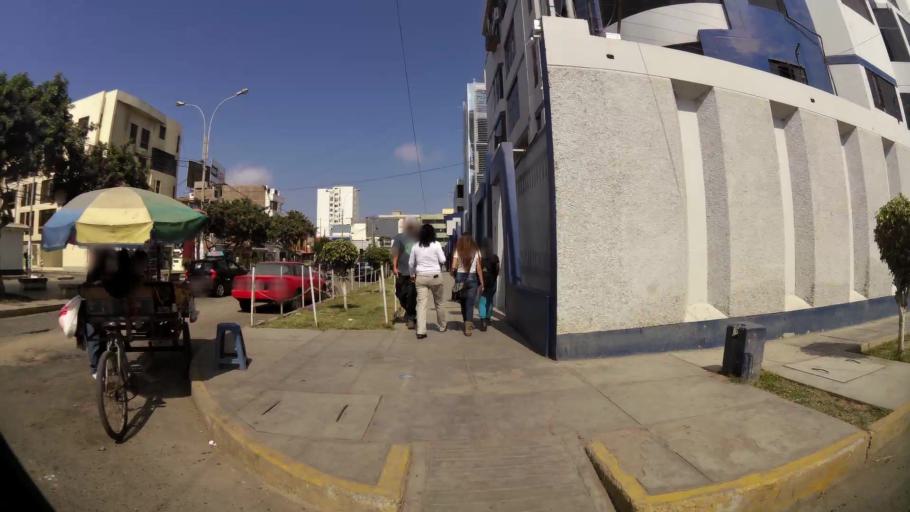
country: PE
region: La Libertad
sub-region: Provincia de Trujillo
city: Buenos Aires
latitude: -8.1281
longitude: -79.0433
